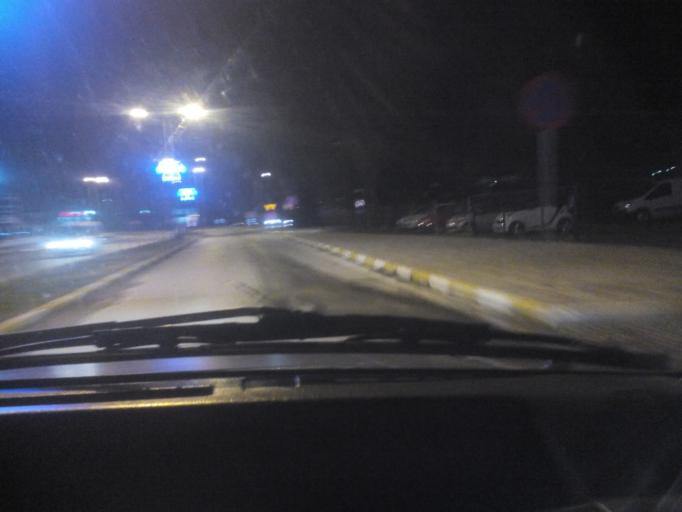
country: GR
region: Central Macedonia
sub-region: Nomos Pellis
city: Aridaia
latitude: 40.9701
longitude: 22.0566
